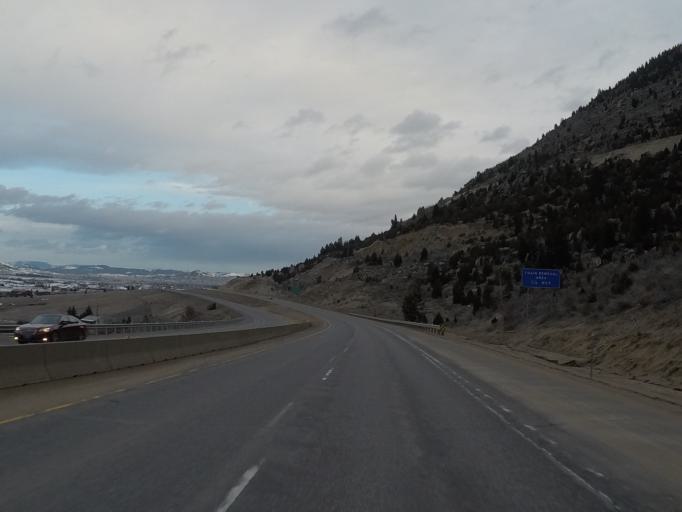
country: US
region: Montana
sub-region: Silver Bow County
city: Butte
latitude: 45.9398
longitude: -112.4572
